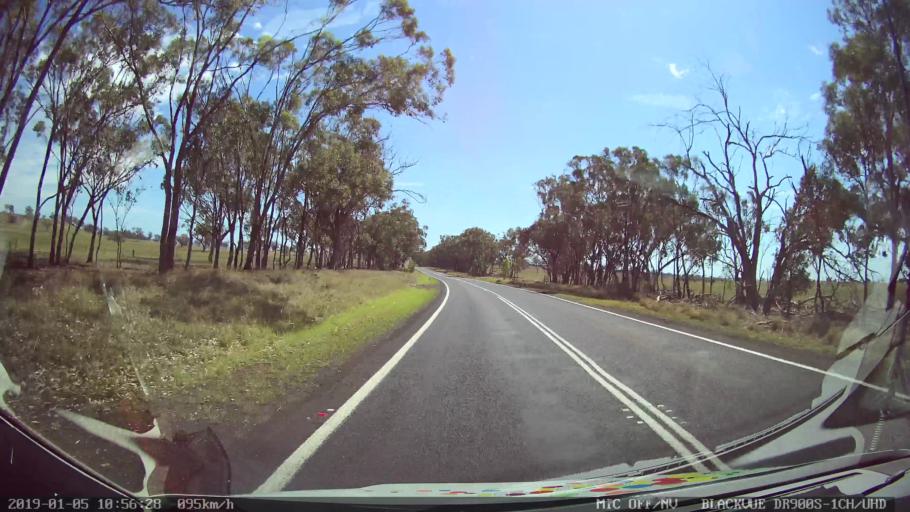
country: AU
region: New South Wales
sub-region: Warrumbungle Shire
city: Coonabarabran
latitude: -31.4411
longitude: 149.1584
